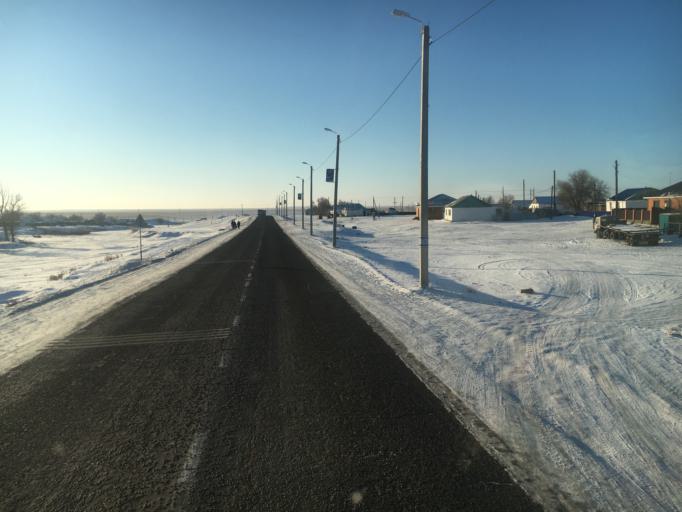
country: KZ
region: Aqtoebe
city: Khromtau
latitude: 50.1251
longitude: 59.0963
